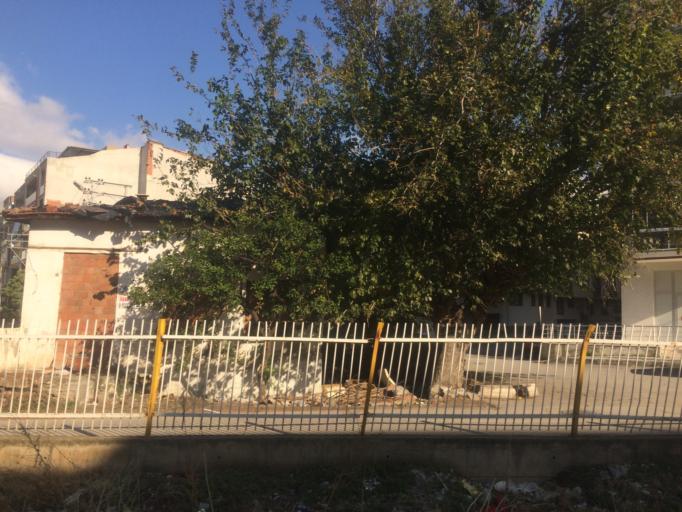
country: TR
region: Izmir
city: Karsiyaka
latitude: 38.4726
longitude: 27.0922
